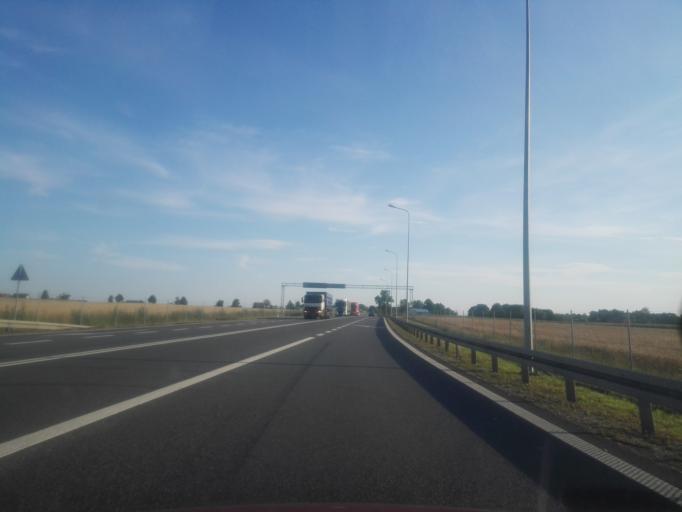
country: PL
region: Lodz Voivodeship
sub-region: Powiat wieruszowski
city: Walichnowy
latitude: 51.3134
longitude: 18.3847
